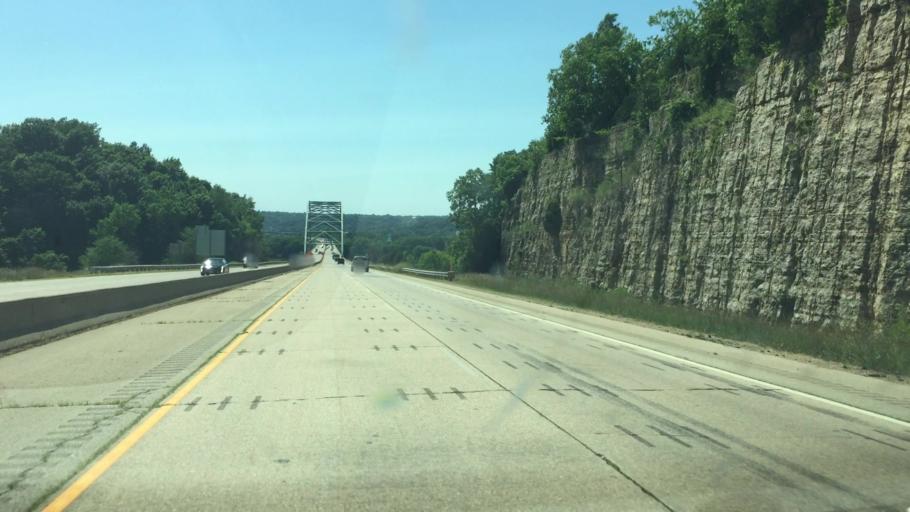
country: US
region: Illinois
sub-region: Jo Daviess County
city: East Dubuque
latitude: 42.5154
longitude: -90.6271
